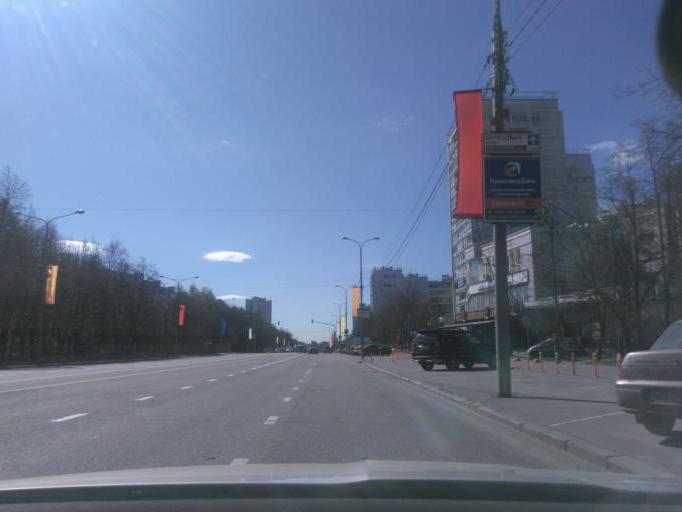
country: RU
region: Moscow
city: Zelenograd
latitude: 55.9996
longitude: 37.2101
